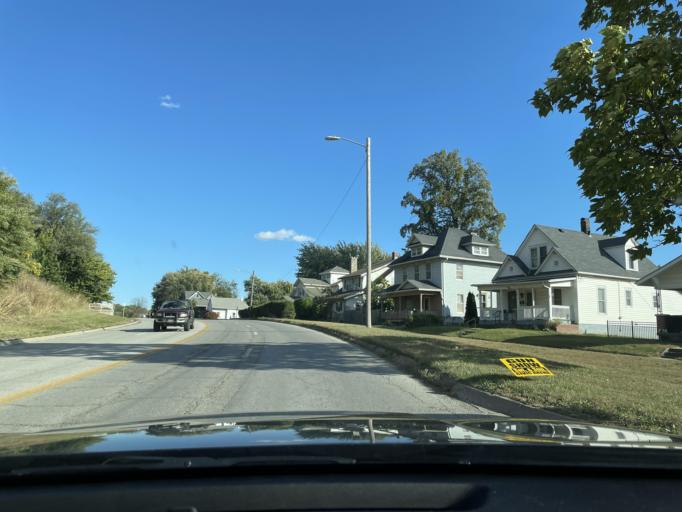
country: US
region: Kansas
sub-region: Doniphan County
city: Elwood
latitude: 39.7118
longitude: -94.8610
